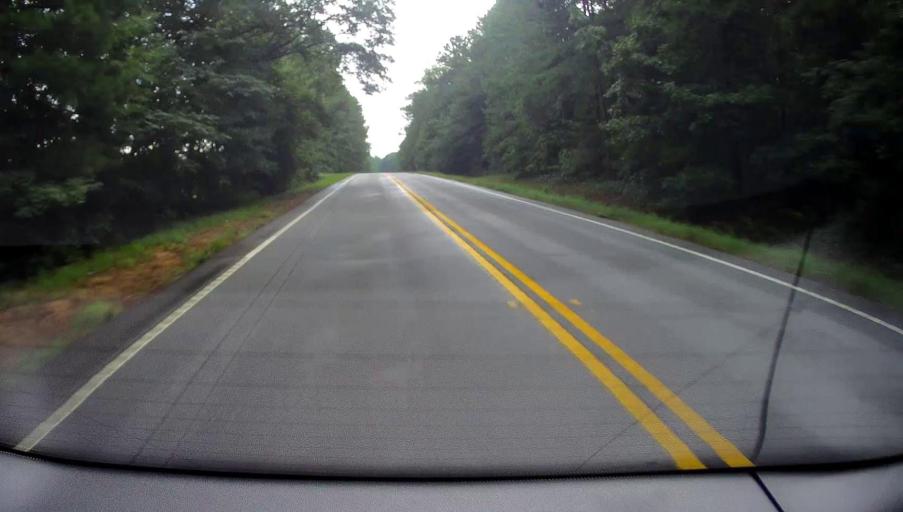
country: US
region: Georgia
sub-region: Coweta County
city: Senoia
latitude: 33.2675
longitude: -84.5549
